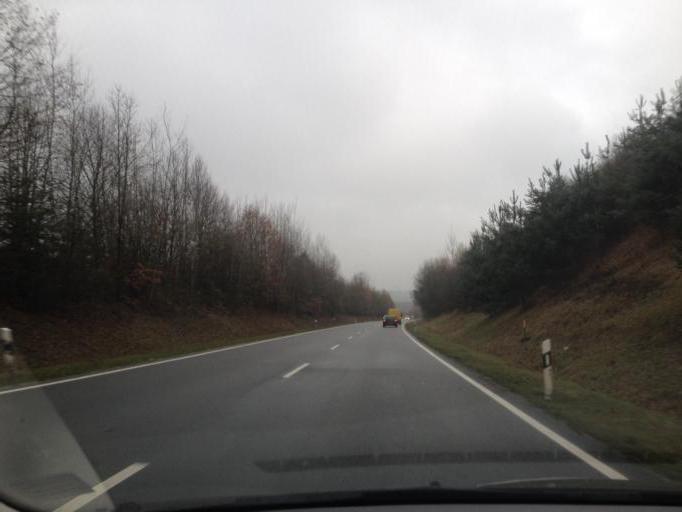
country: DE
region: Bavaria
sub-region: Regierungsbezirk Mittelfranken
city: Heroldsberg
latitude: 49.5322
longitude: 11.1689
